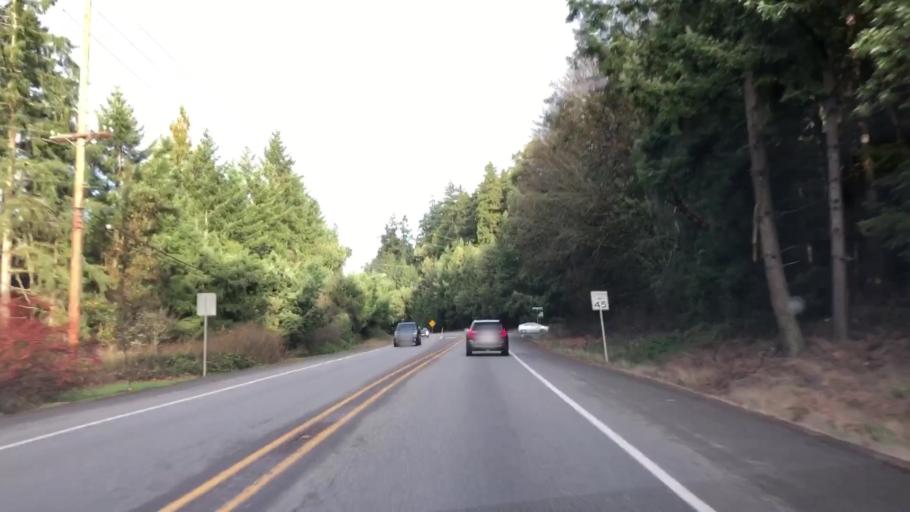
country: US
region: Washington
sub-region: Kitsap County
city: Suquamish
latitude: 47.7026
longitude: -122.5583
